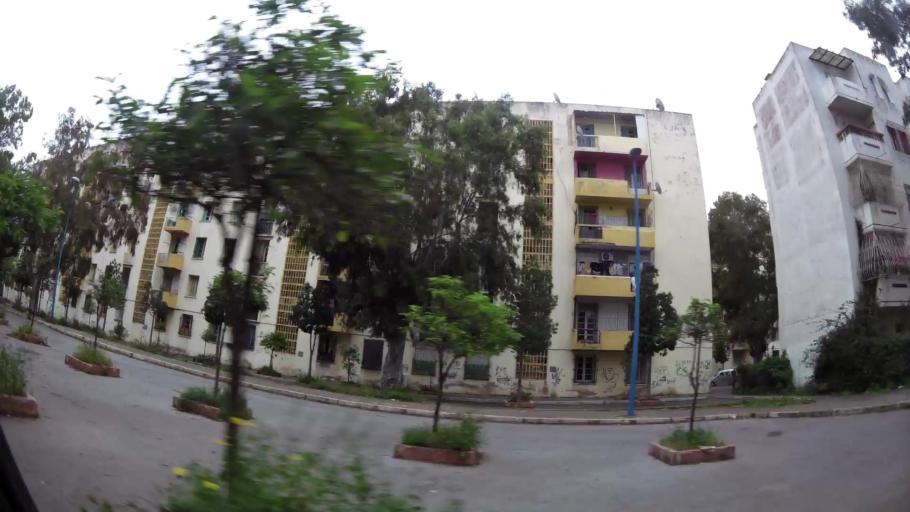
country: MA
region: Grand Casablanca
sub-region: Casablanca
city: Casablanca
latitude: 33.5711
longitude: -7.5584
